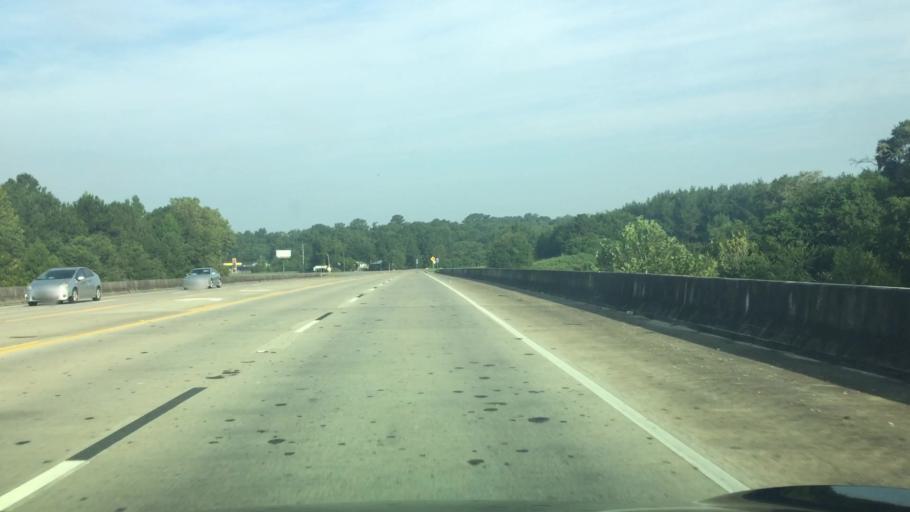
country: US
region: Alabama
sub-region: Covington County
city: Andalusia
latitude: 31.3479
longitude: -86.5292
